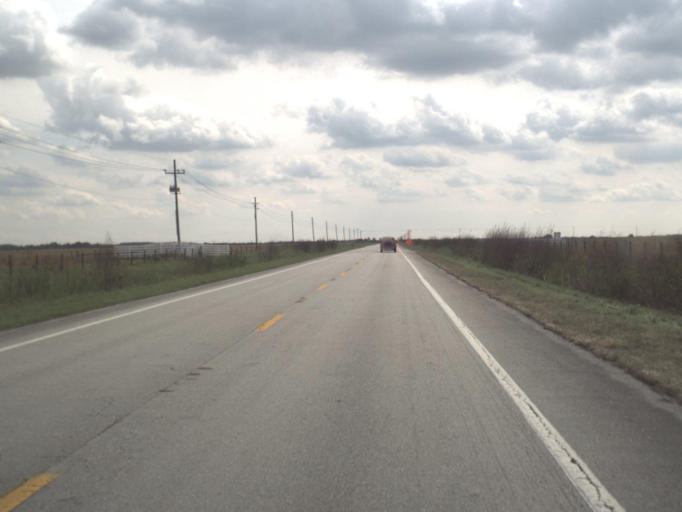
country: US
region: Florida
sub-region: Okeechobee County
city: Cypress Quarters
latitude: 27.4731
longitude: -80.8079
